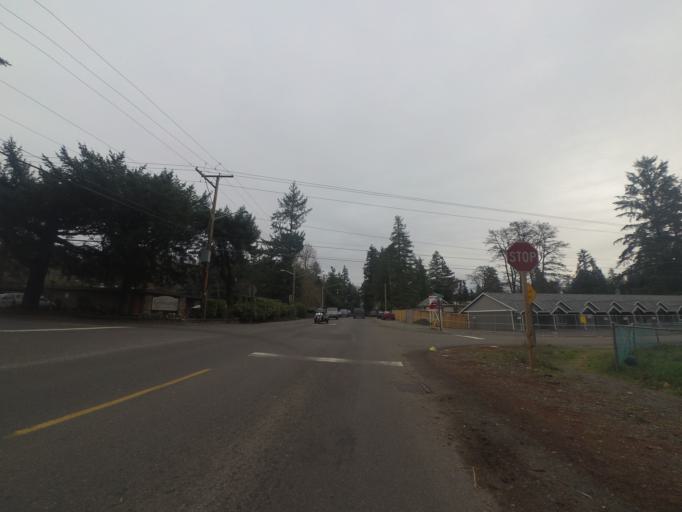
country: US
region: Washington
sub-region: Pierce County
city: McChord Air Force Base
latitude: 47.1212
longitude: -122.5265
